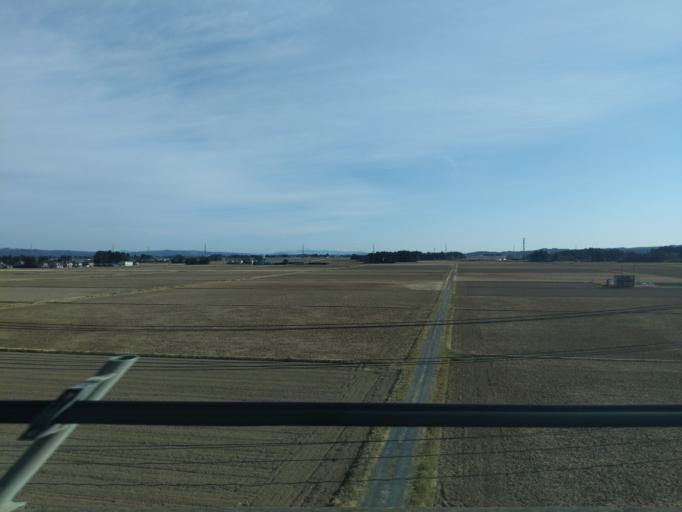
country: JP
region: Miyagi
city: Furukawa
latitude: 38.5503
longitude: 140.9625
